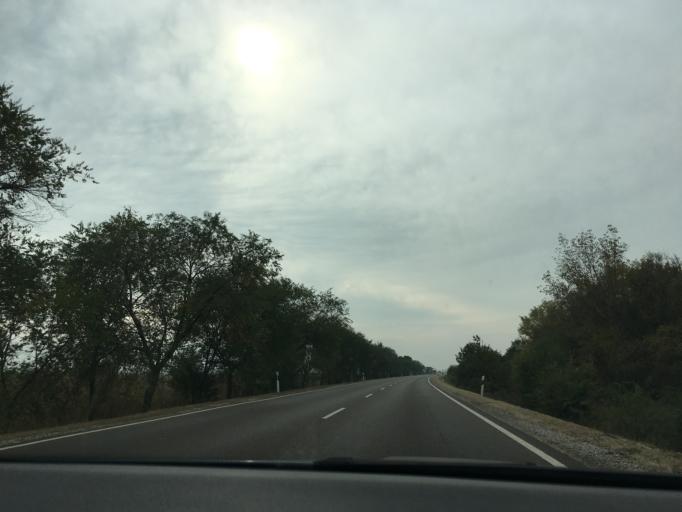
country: HU
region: Jasz-Nagykun-Szolnok
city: Kisujszallas
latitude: 47.2542
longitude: 20.8419
